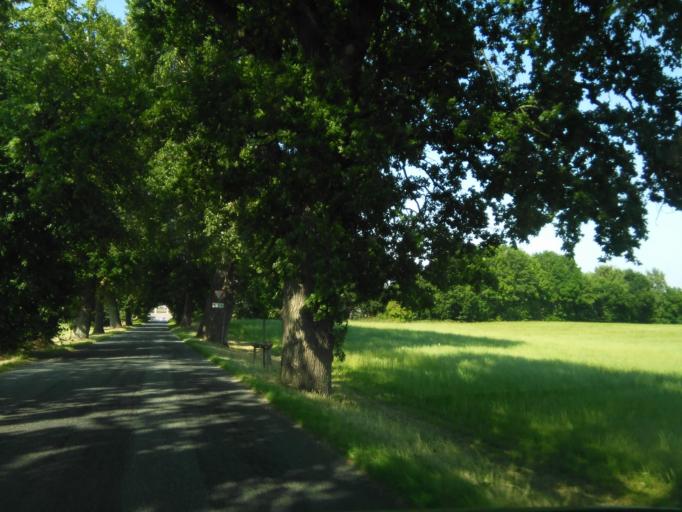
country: DK
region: Central Jutland
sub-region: Arhus Kommune
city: Kolt
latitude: 56.1363
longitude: 10.0775
